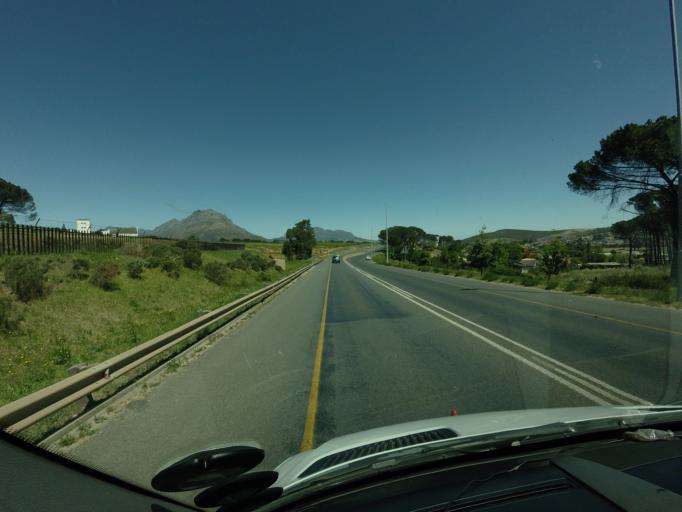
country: ZA
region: Western Cape
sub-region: Cape Winelands District Municipality
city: Stellenbosch
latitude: -33.9072
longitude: 18.8594
